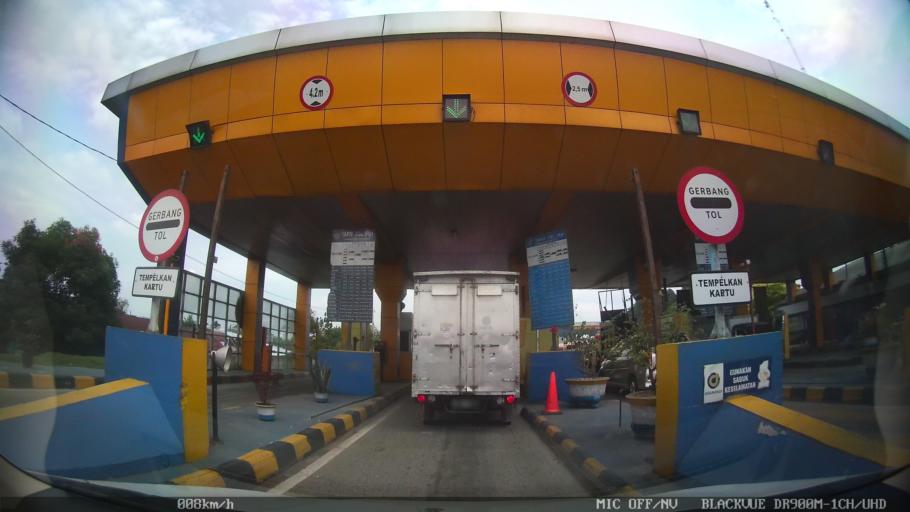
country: ID
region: North Sumatra
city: Medan
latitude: 3.6457
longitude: 98.6801
